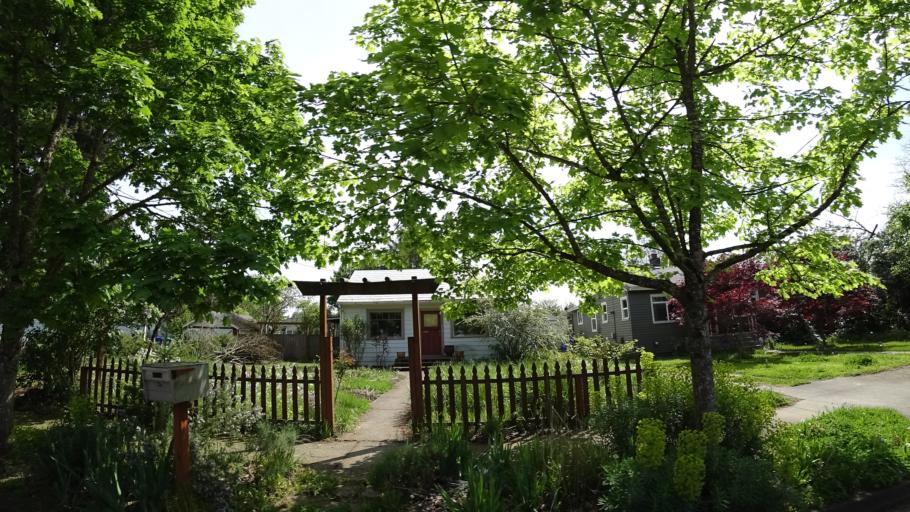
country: US
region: Oregon
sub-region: Clackamas County
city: Milwaukie
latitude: 45.4727
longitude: -122.6084
